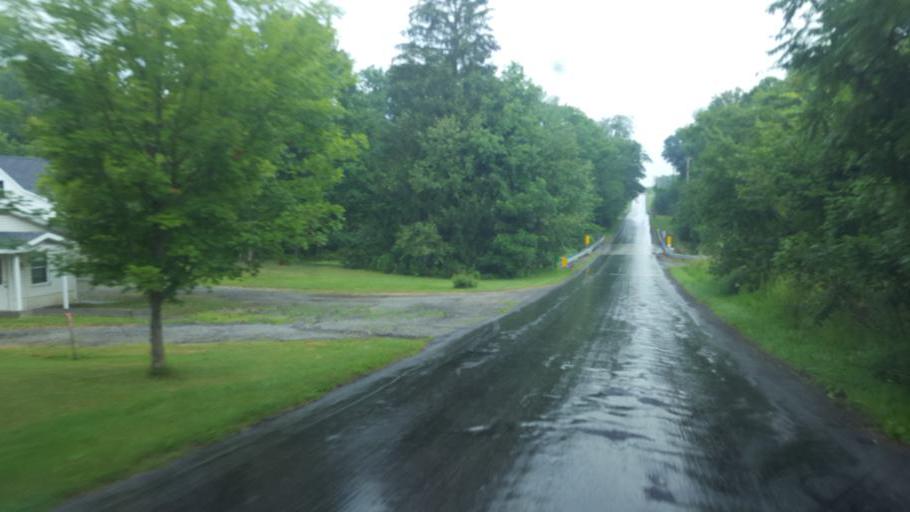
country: US
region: Ohio
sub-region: Geauga County
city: Middlefield
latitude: 41.4537
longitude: -80.9852
